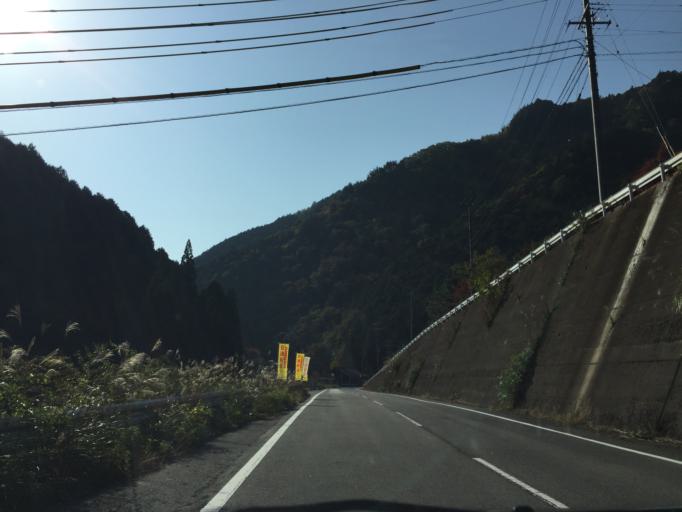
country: JP
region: Gifu
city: Minokamo
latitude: 35.5544
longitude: 137.1154
